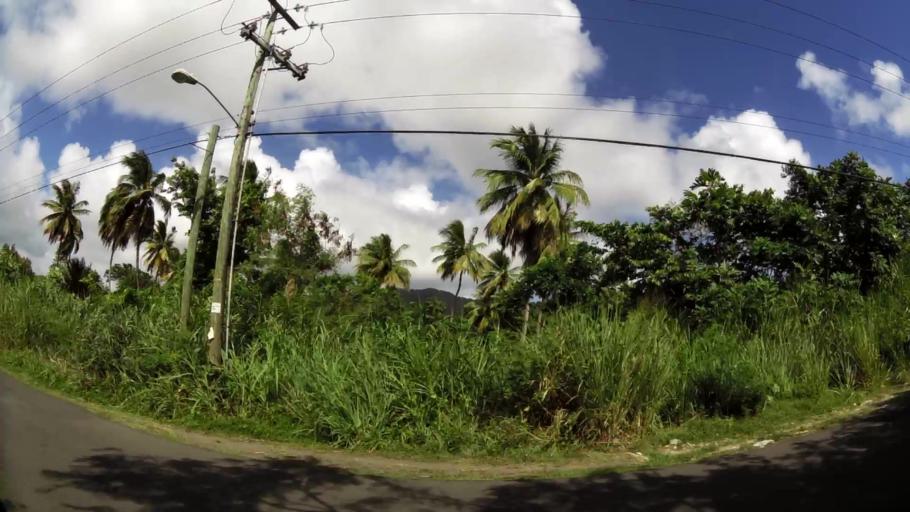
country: LC
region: Dennery Quarter
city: Dennery
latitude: 13.9362
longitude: -60.9148
